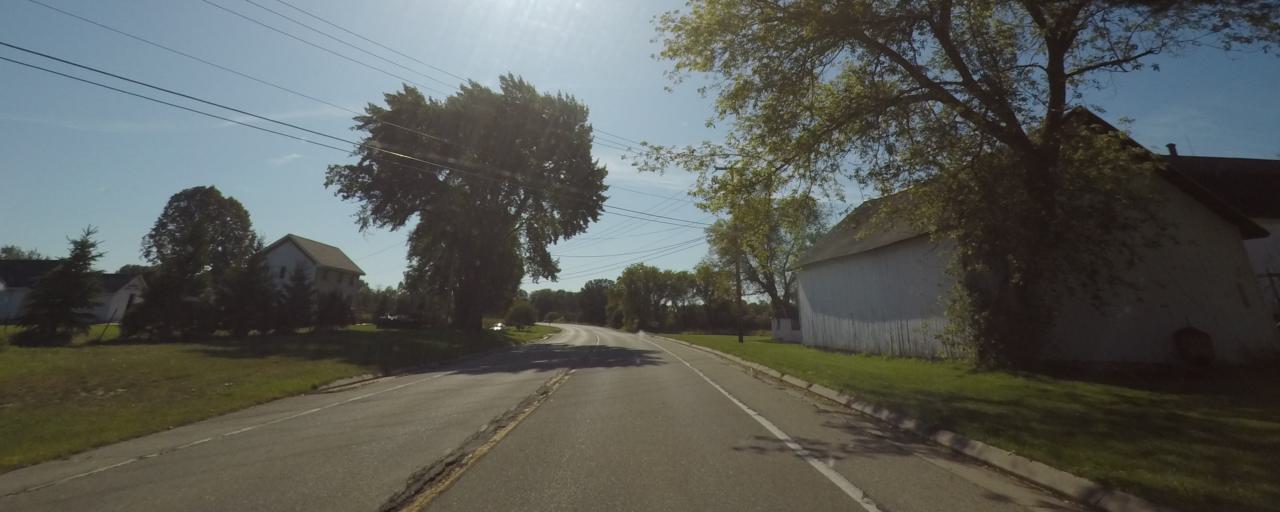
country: US
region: Wisconsin
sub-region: Waukesha County
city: Dousman
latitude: 43.0236
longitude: -88.5017
